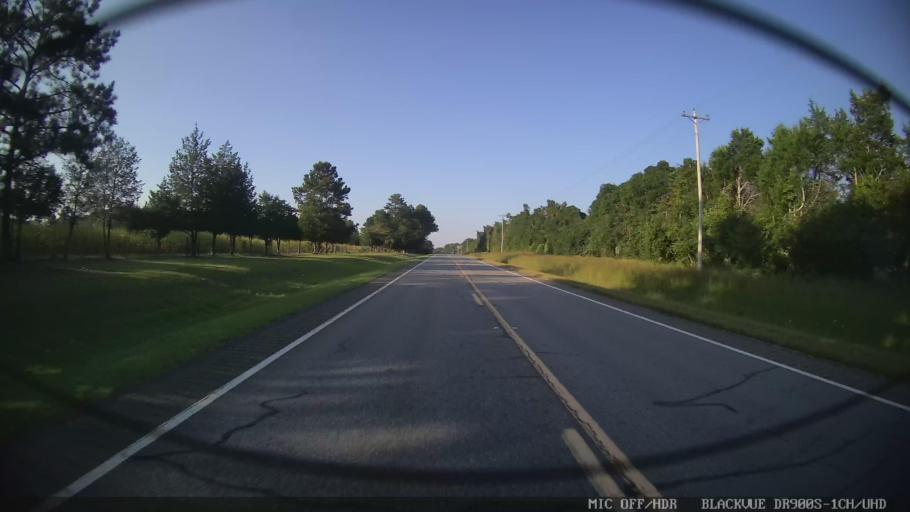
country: US
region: Tennessee
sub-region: Bradley County
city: Wildwood Lake
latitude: 34.9623
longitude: -84.7342
